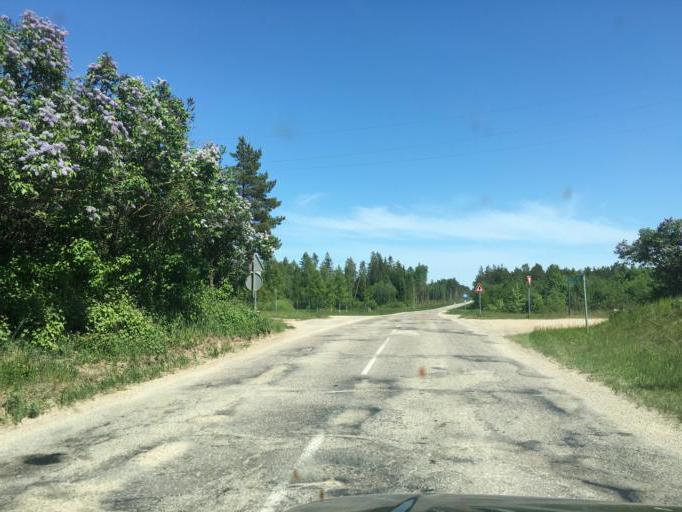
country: LV
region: Talsu Rajons
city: Valdemarpils
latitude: 57.4488
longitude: 22.6525
